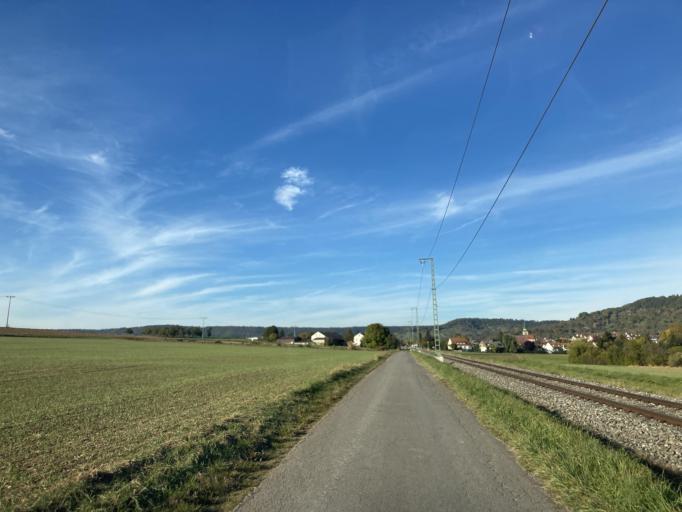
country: DE
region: Baden-Wuerttemberg
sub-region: Tuebingen Region
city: Rottenburg
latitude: 48.5451
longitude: 8.9635
